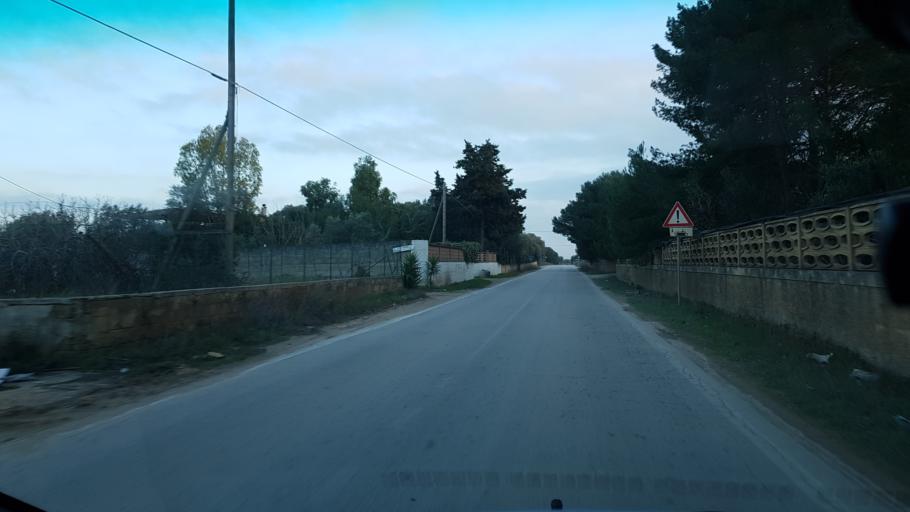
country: IT
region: Apulia
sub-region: Provincia di Brindisi
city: San Vito dei Normanni
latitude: 40.6433
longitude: 17.7778
